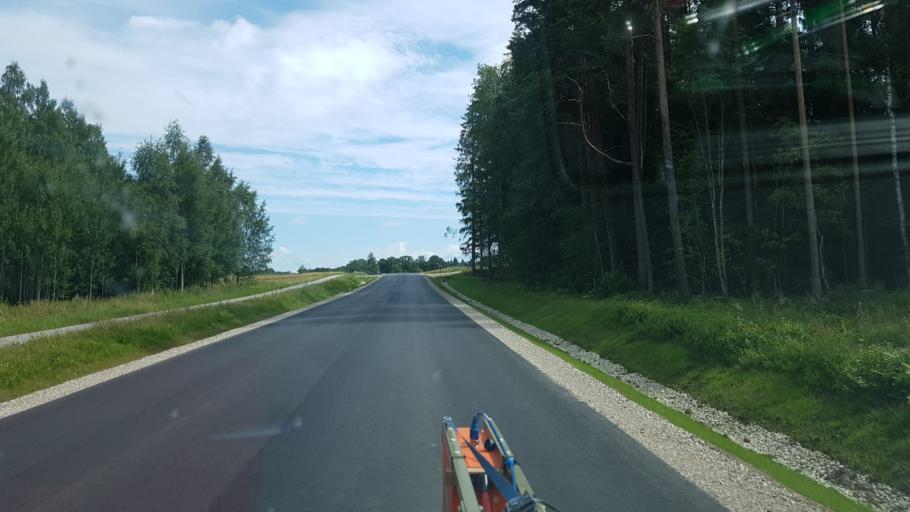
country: EE
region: Viljandimaa
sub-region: Suure-Jaani vald
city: Suure-Jaani
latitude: 58.5390
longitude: 25.5122
